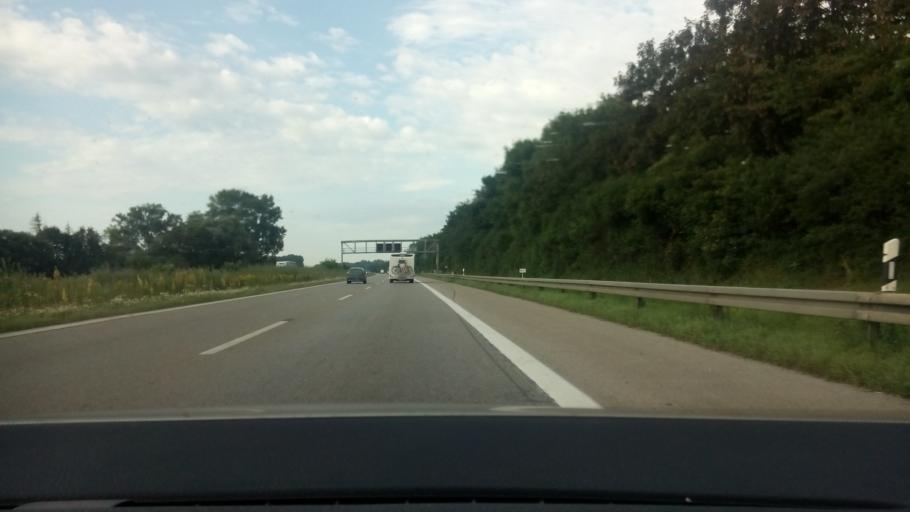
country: DE
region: Bavaria
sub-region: Upper Bavaria
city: Oberschleissheim
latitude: 48.2659
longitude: 11.5380
